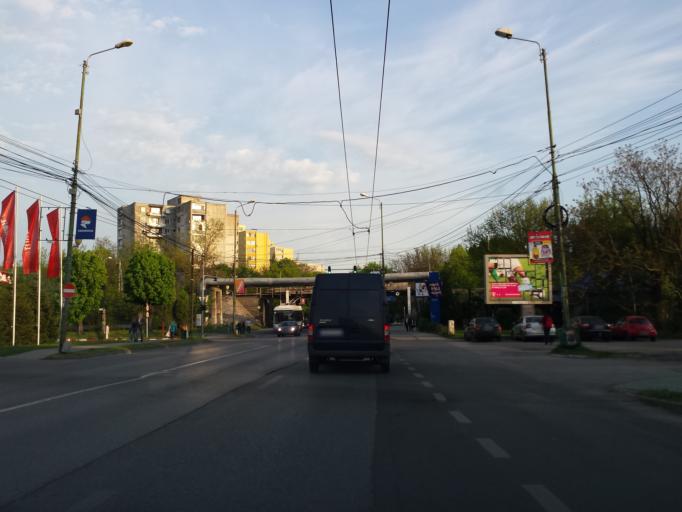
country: RO
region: Timis
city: Timisoara
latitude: 45.7629
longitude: 21.2259
